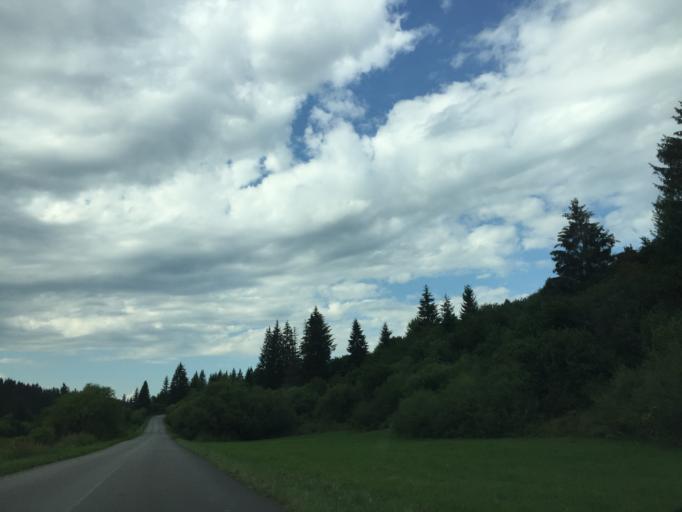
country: SK
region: Zilinsky
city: Namestovo
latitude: 49.4031
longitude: 19.3331
